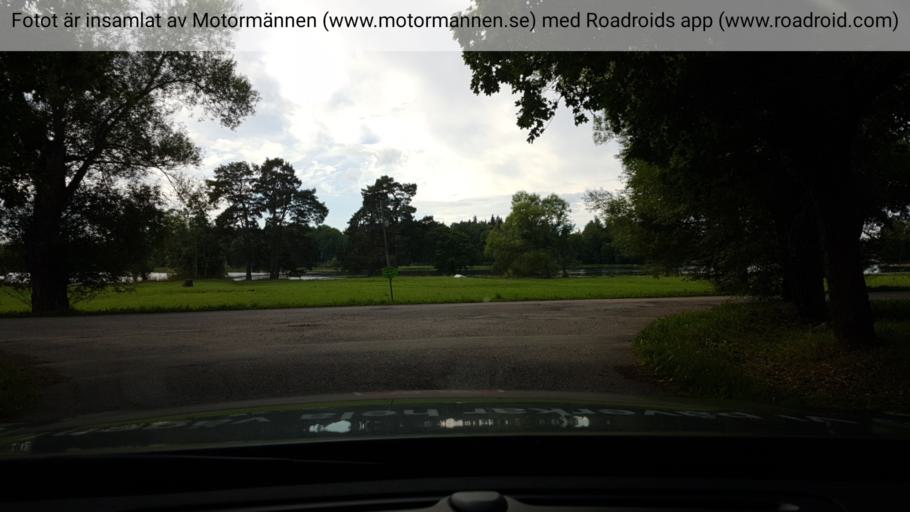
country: SE
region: Uppsala
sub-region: Heby Kommun
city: Tarnsjo
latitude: 60.2889
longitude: 16.8908
